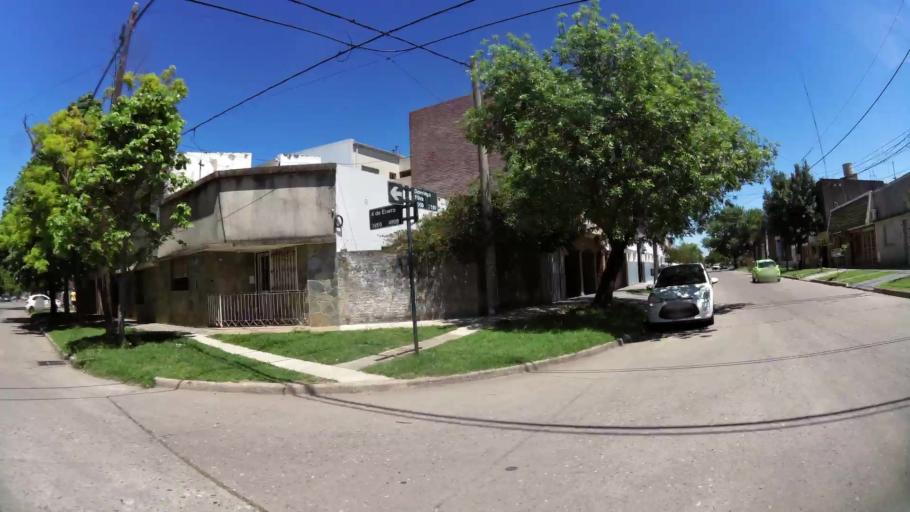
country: AR
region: Santa Fe
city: Santa Fe de la Vera Cruz
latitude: -31.6299
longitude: -60.7073
